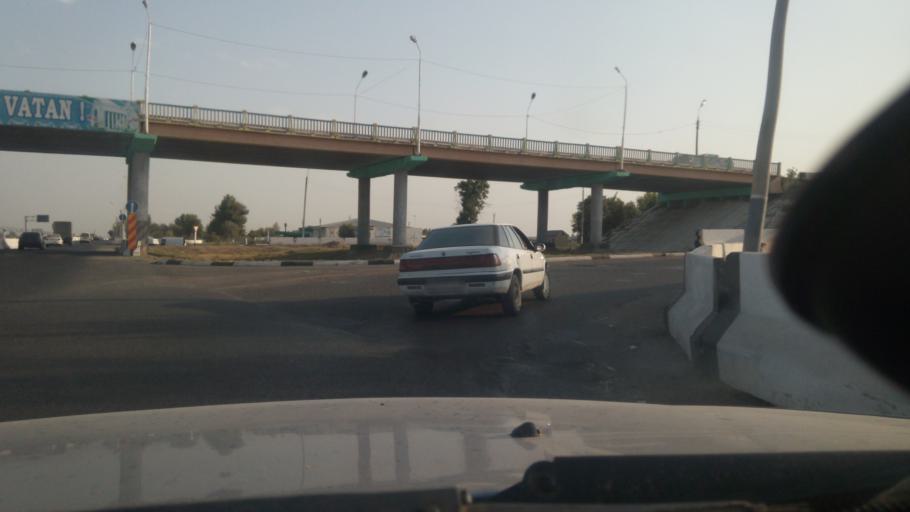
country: UZ
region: Sirdaryo
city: Guliston
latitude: 40.4748
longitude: 68.7703
